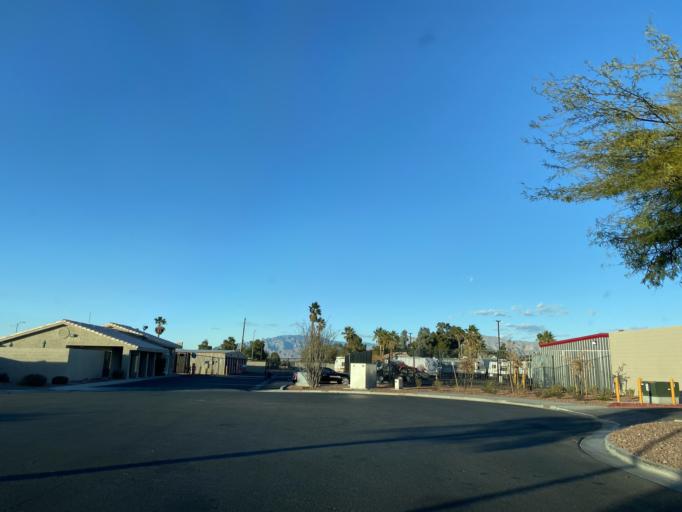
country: US
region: Nevada
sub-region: Clark County
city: Spring Valley
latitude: 36.2189
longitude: -115.2559
